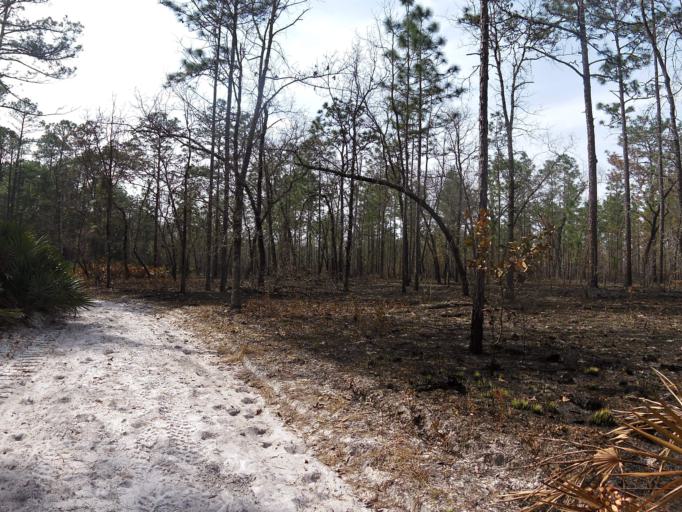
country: US
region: Florida
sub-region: Clay County
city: Middleburg
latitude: 30.1274
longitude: -81.8992
